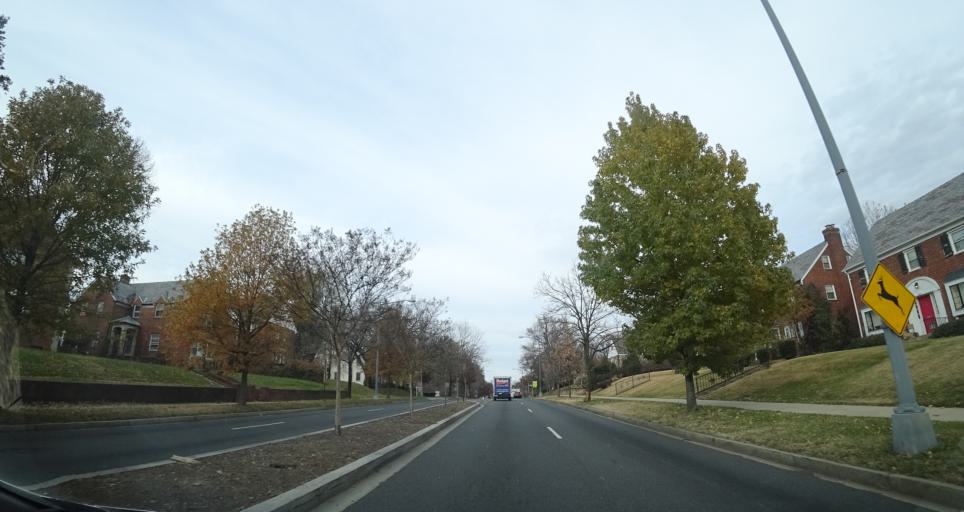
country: US
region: Maryland
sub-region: Montgomery County
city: Silver Spring
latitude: 38.9890
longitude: -77.0363
